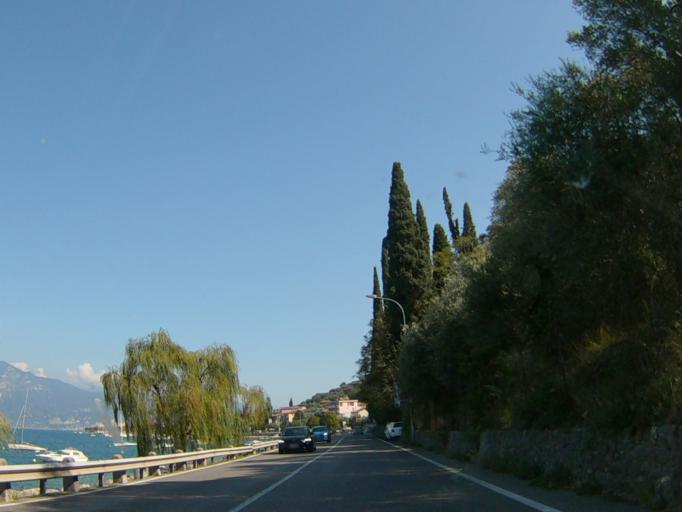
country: IT
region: Veneto
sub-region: Provincia di Verona
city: Torri del Benaco
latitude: 45.5976
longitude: 10.6839
